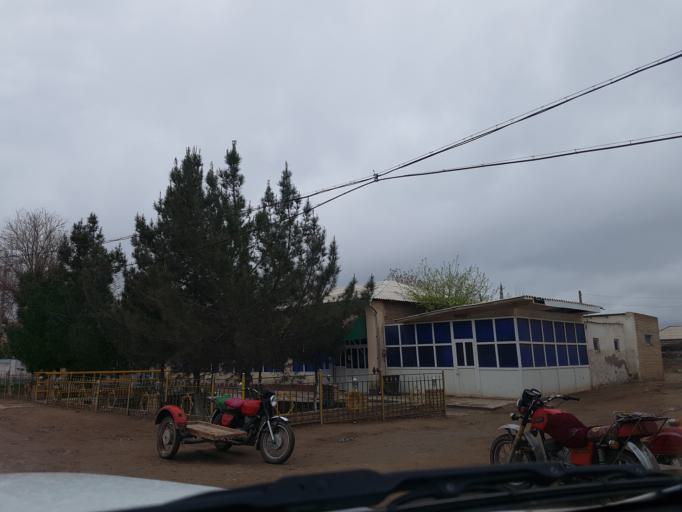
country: TM
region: Lebap
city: Sayat
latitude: 38.4546
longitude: 64.3800
